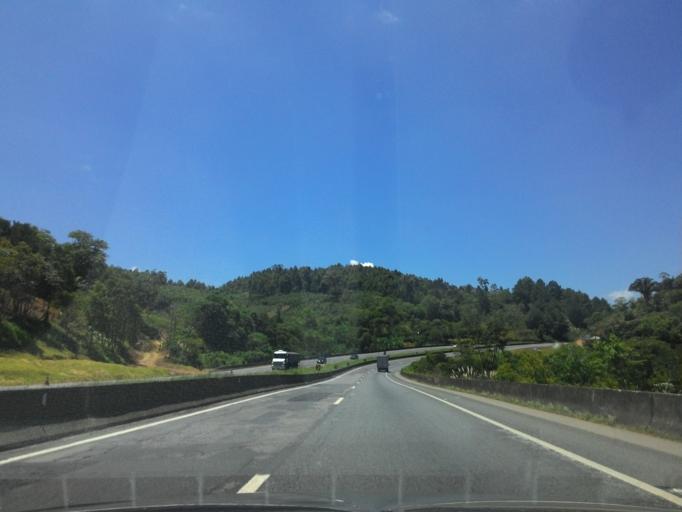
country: BR
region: Parana
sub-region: Antonina
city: Antonina
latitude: -25.0669
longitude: -48.5806
